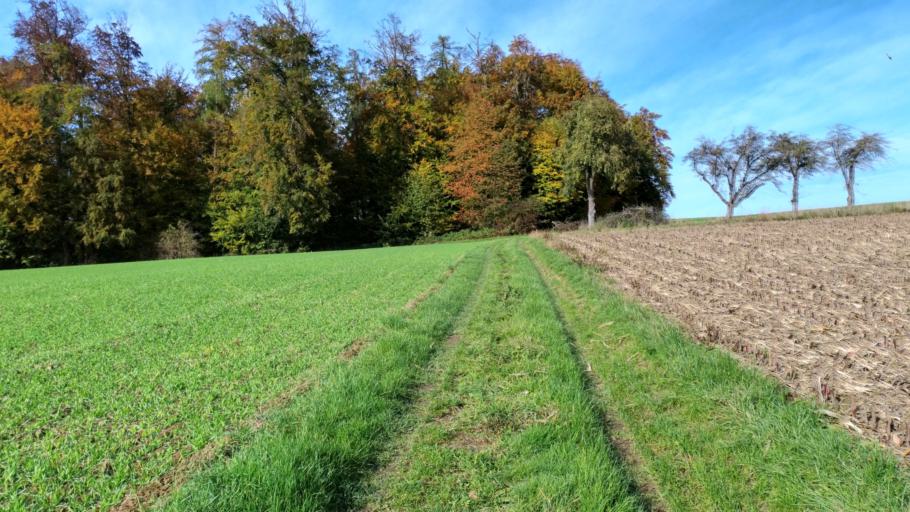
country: DE
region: Baden-Wuerttemberg
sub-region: Karlsruhe Region
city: Binau
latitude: 49.3737
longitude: 9.0381
